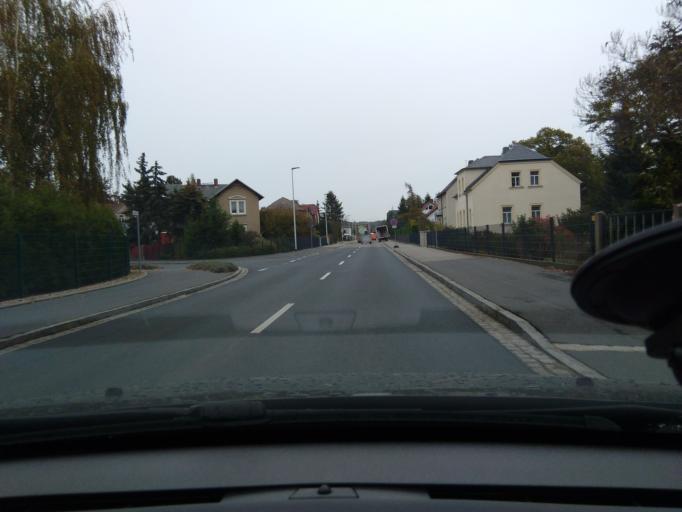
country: DE
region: Saxony
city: Weinbohla
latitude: 51.1498
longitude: 13.5593
